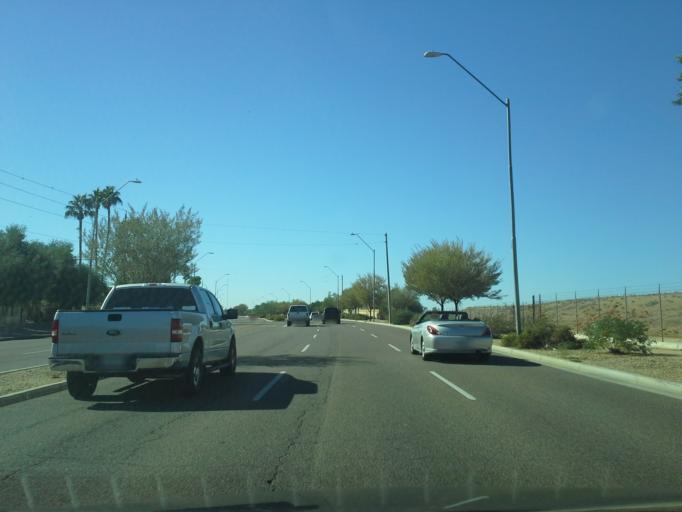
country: US
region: Arizona
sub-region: Maricopa County
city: Paradise Valley
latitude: 33.6403
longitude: -111.9351
